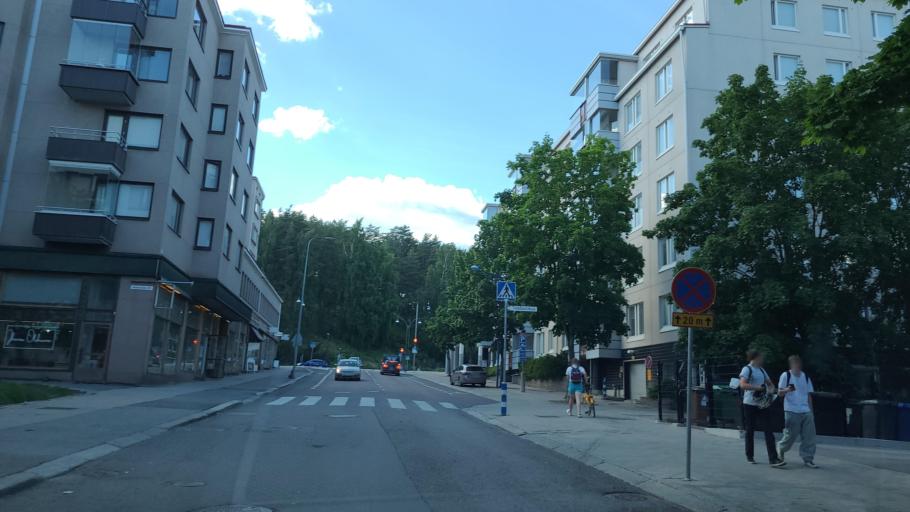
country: FI
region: Central Finland
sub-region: Jyvaeskylae
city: Jyvaeskylae
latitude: 62.2419
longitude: 25.7443
